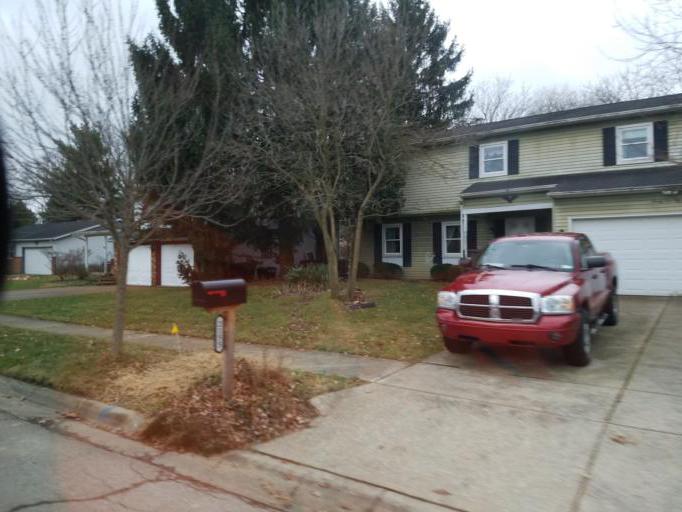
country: US
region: Ohio
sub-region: Franklin County
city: Minerva Park
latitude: 40.0778
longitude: -82.9602
